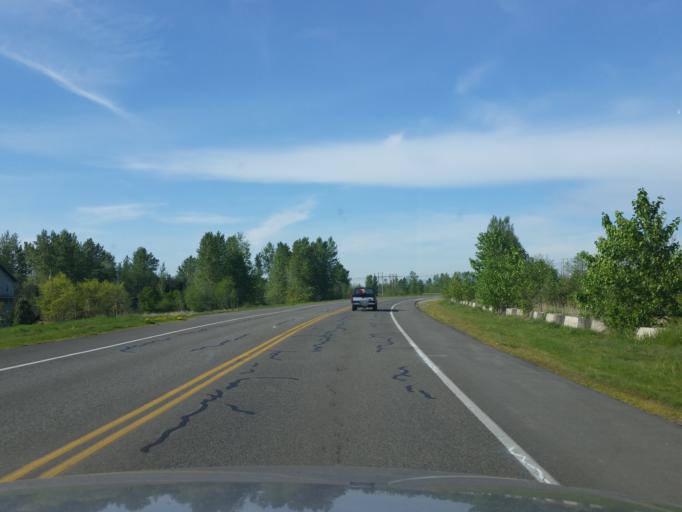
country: US
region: Washington
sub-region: Snohomish County
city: Fobes Hill
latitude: 47.9326
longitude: -122.1722
